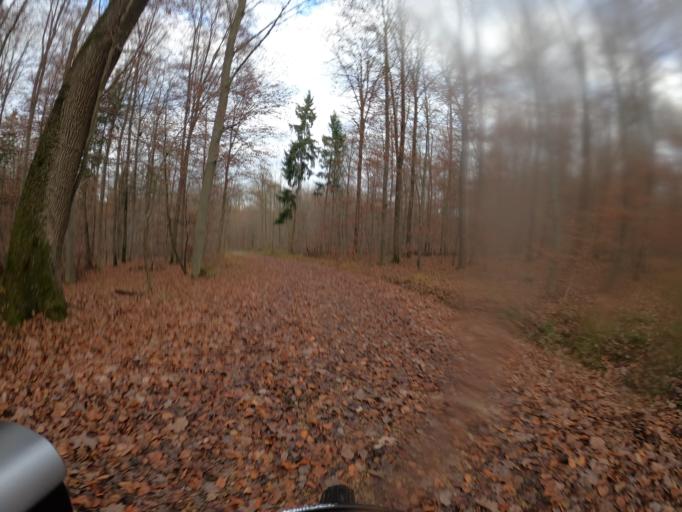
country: DE
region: Baden-Wuerttemberg
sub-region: Regierungsbezirk Stuttgart
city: Notzingen
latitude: 48.6813
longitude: 9.4425
